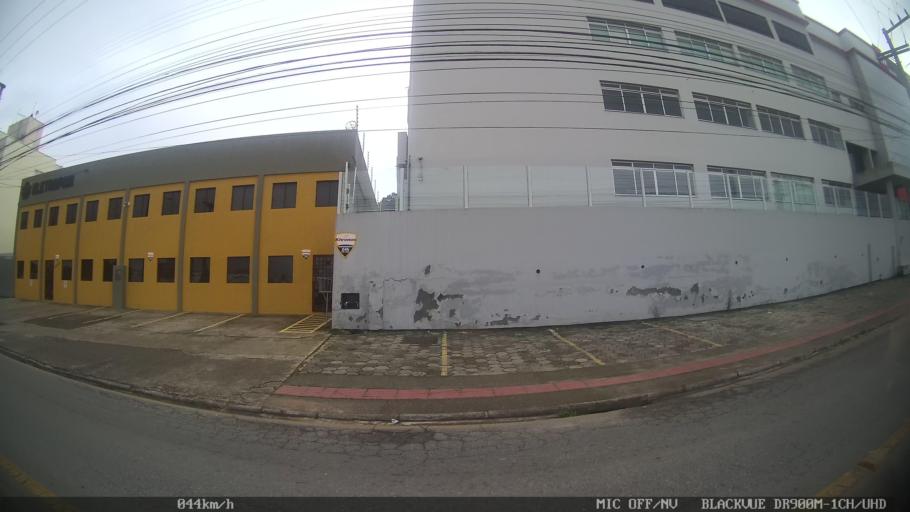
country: BR
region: Santa Catarina
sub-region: Sao Jose
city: Campinas
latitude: -27.5870
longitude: -48.6202
